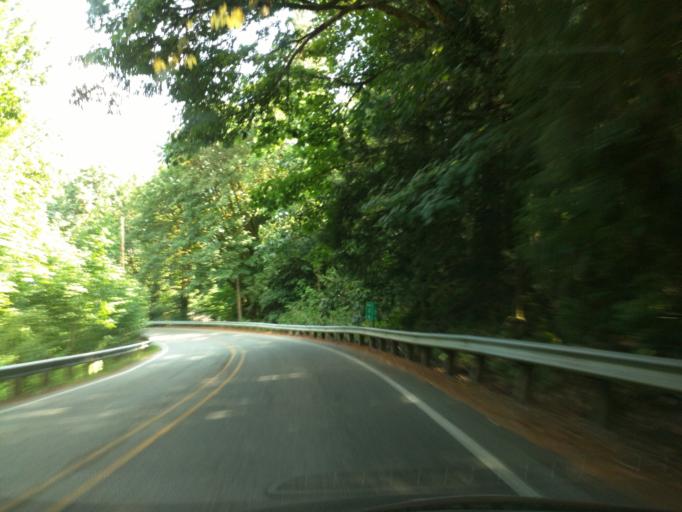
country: US
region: Washington
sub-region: Whatcom County
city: Peaceful Valley
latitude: 48.9226
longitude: -122.0746
